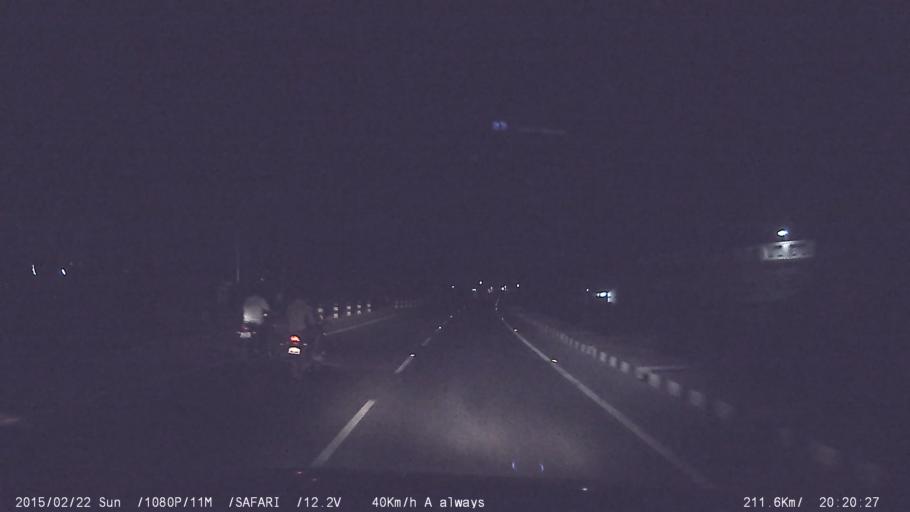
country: IN
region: Tamil Nadu
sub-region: Dindigul
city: Nilakottai
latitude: 10.2838
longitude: 77.8730
